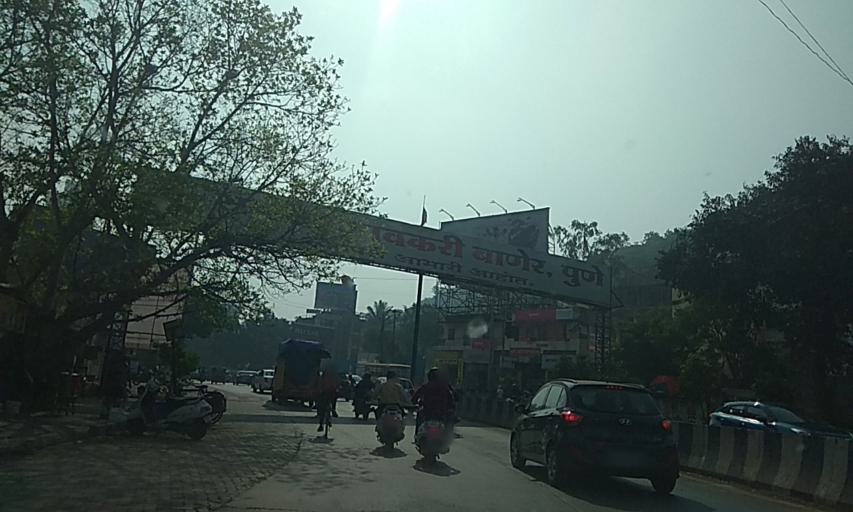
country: IN
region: Maharashtra
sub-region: Pune Division
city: Khadki
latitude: 18.5603
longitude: 73.7886
